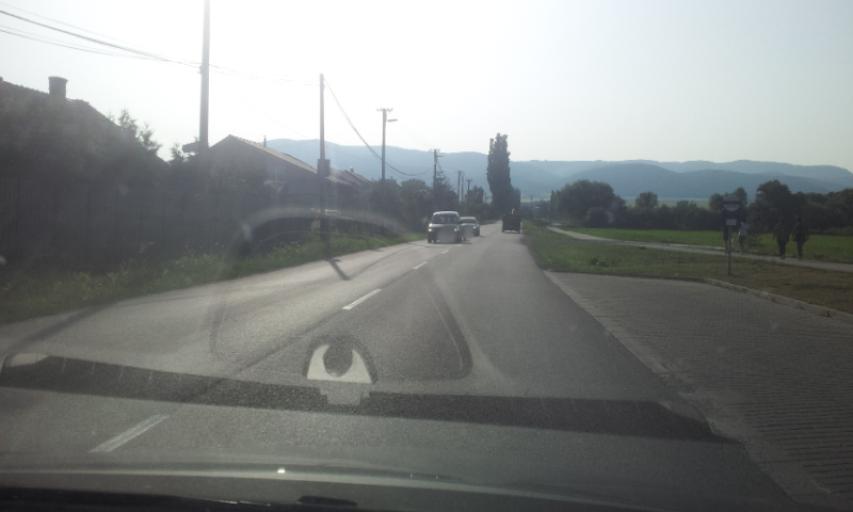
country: SK
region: Kosicky
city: Kosice
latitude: 48.6069
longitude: 21.3327
